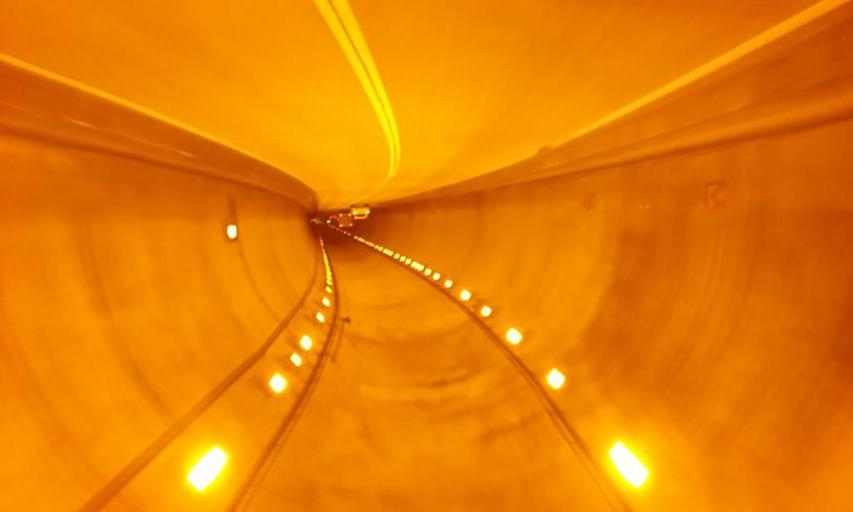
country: JP
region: Kyoto
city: Kameoka
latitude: 35.2298
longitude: 135.5743
